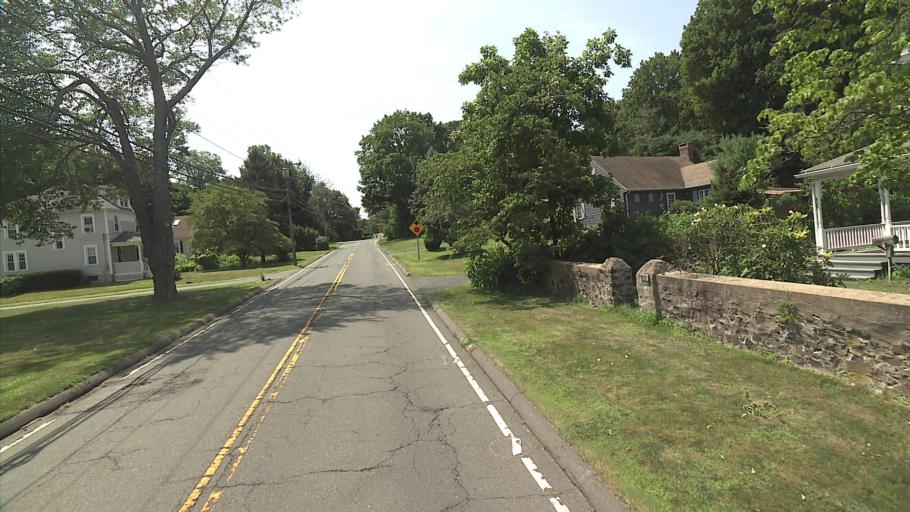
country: US
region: Connecticut
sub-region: Hartford County
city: Kensington
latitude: 41.6242
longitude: -72.7826
